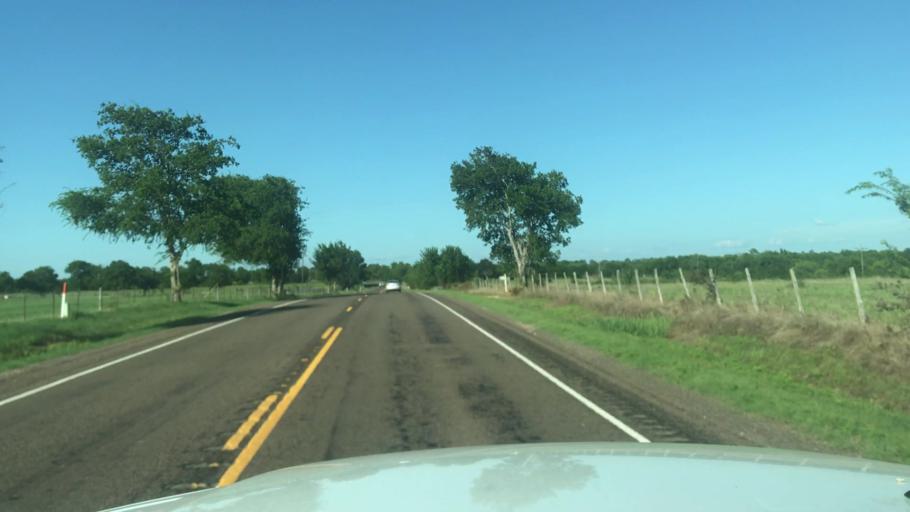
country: US
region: Texas
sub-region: Grimes County
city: Anderson
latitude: 30.6305
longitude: -95.8749
